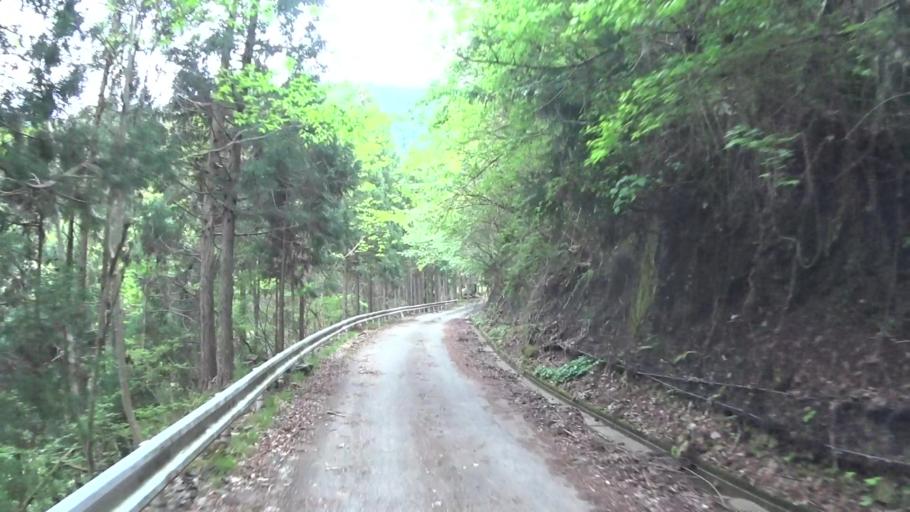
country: JP
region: Kyoto
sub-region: Kyoto-shi
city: Kamigyo-ku
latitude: 35.1786
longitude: 135.7051
